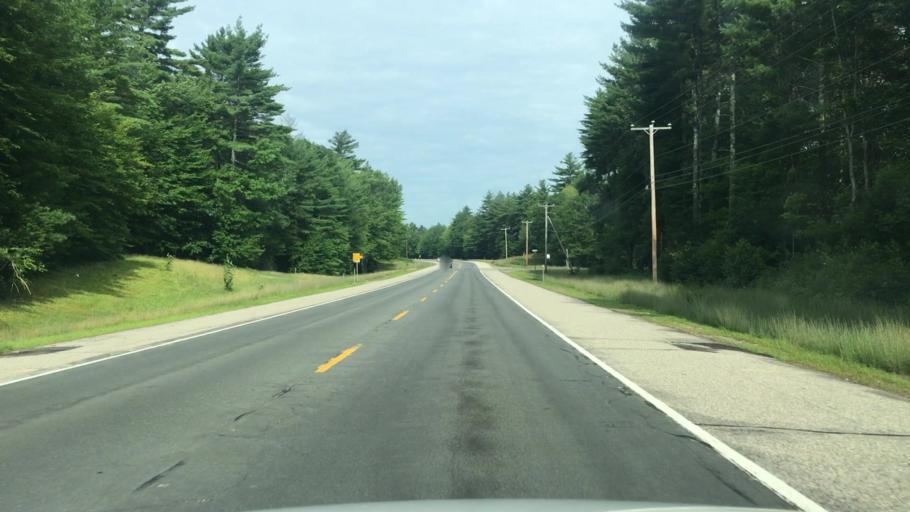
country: US
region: New Hampshire
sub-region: Carroll County
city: Tamworth
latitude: 43.8228
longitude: -71.2223
